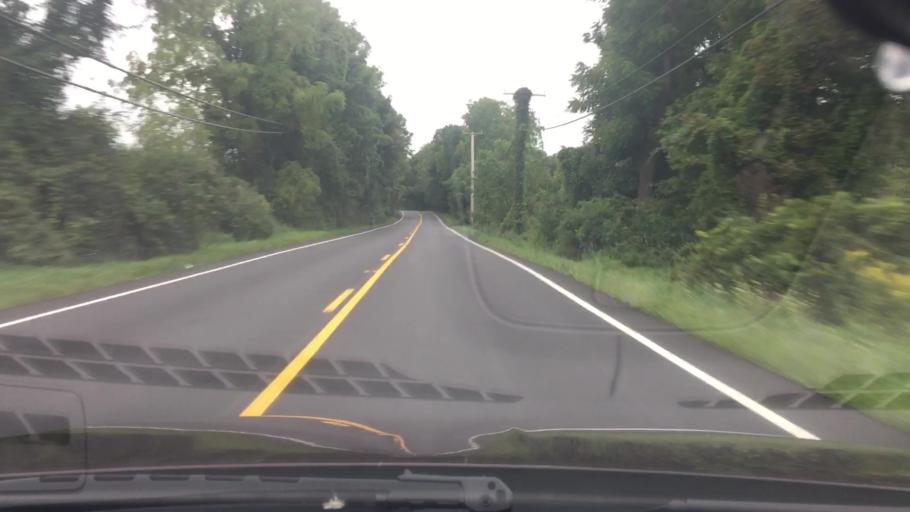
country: US
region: New York
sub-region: Dutchess County
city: Millbrook
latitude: 41.8028
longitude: -73.6398
